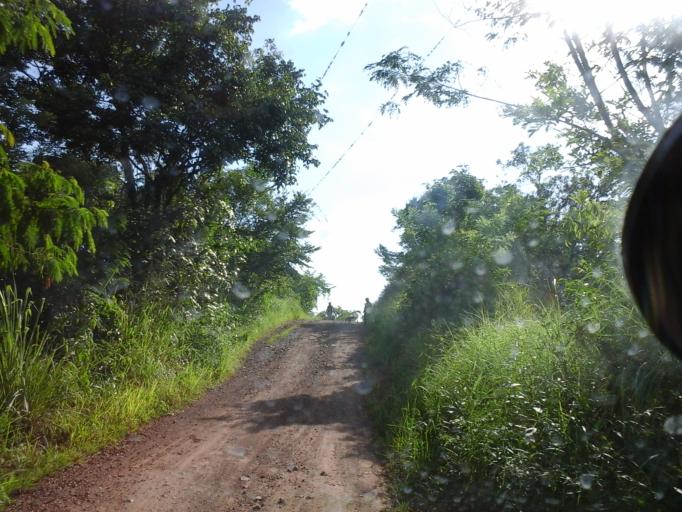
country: CO
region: Cesar
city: San Diego
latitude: 10.2689
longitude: -73.0988
